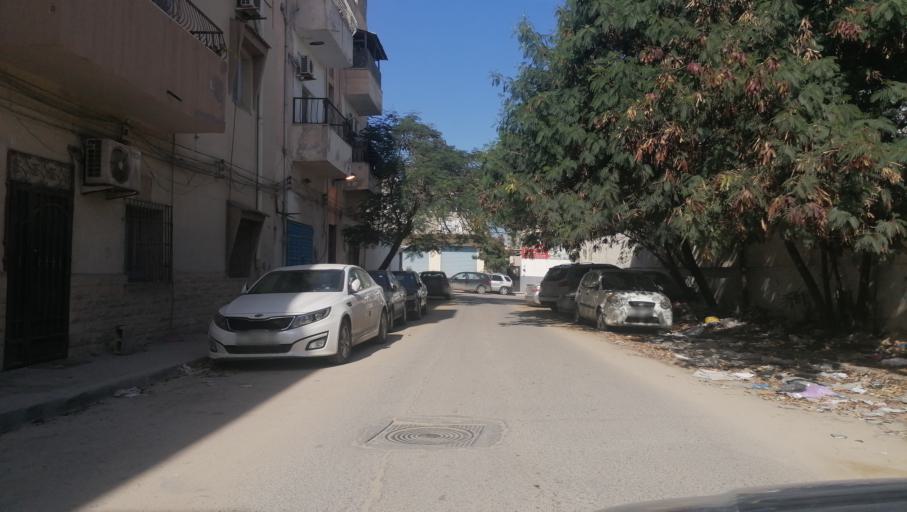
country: LY
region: Tripoli
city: Tripoli
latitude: 32.8913
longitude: 13.1966
